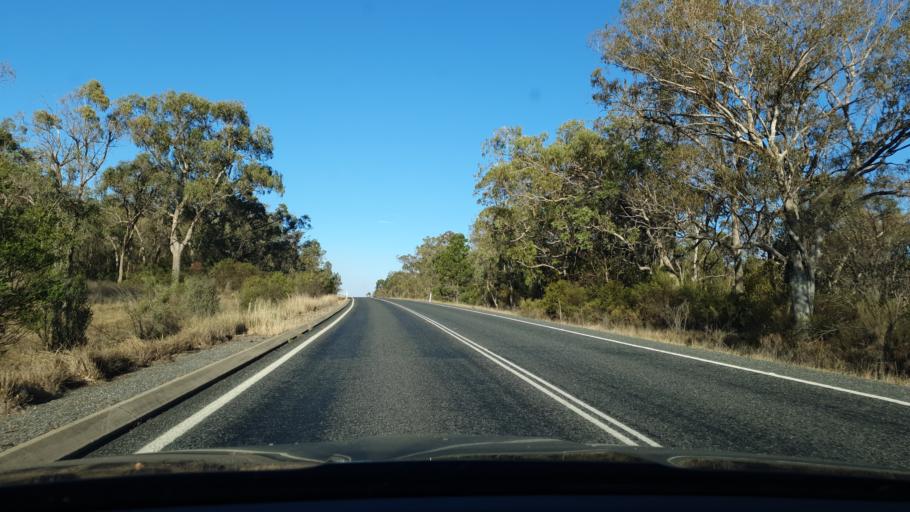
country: AU
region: Queensland
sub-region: Southern Downs
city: Stanthorpe
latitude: -28.6426
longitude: 151.9356
